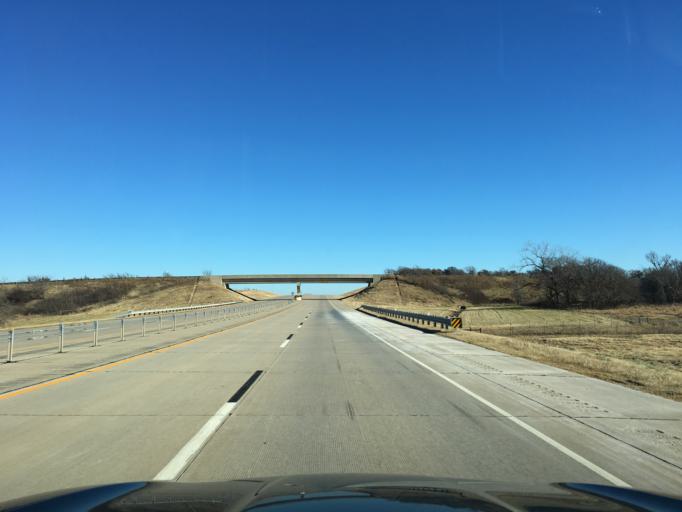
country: US
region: Oklahoma
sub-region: Payne County
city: Yale
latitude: 36.2251
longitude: -96.6448
